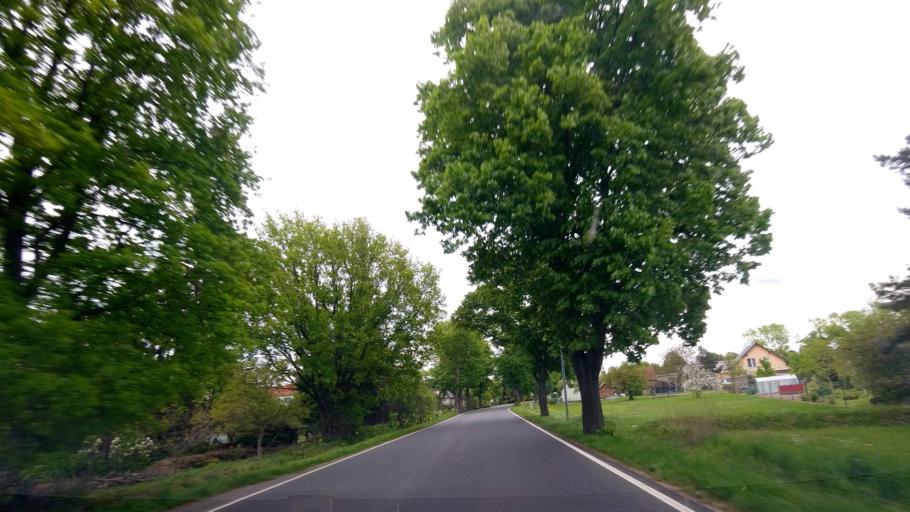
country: DE
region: Brandenburg
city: Drahnsdorf
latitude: 51.8534
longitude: 13.6018
